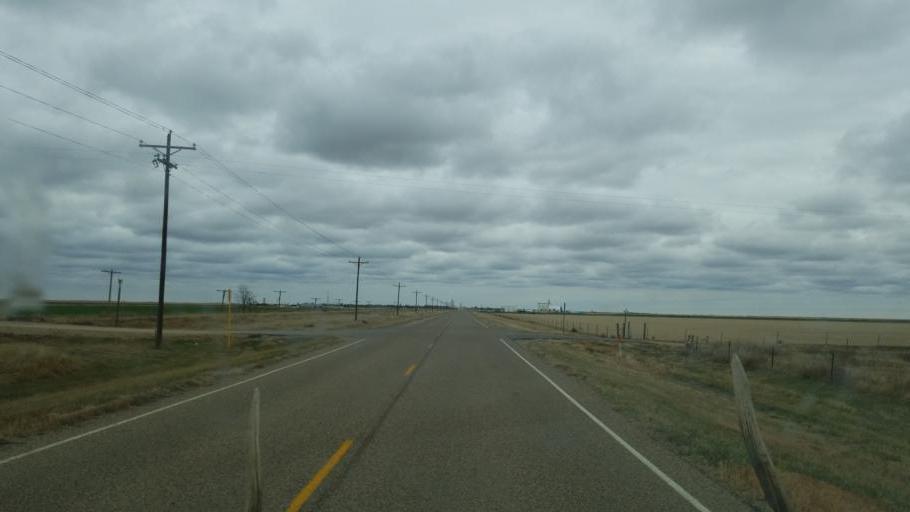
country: US
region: Colorado
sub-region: Kiowa County
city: Eads
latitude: 38.4826
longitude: -102.8235
